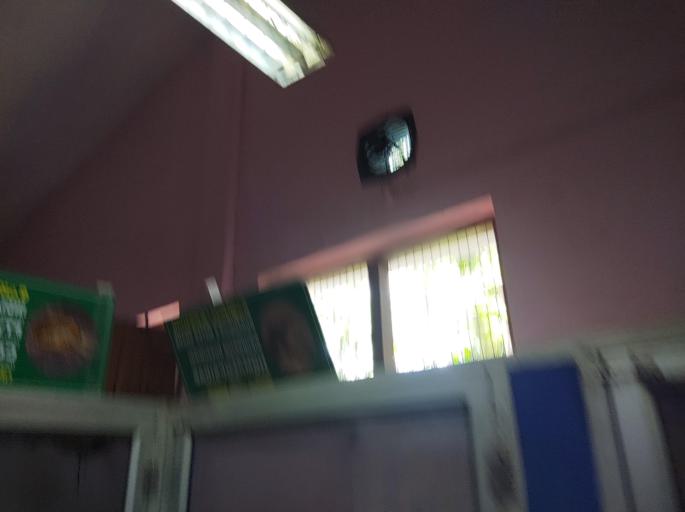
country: IN
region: Kerala
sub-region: Thiruvananthapuram
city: Thiruvananthapuram
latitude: 8.4915
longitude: 76.9749
